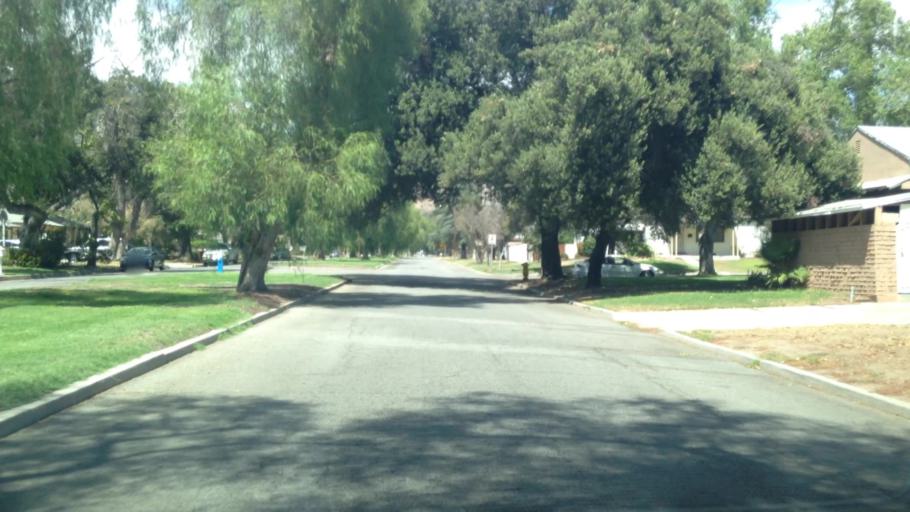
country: US
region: California
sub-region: San Bernardino County
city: San Bernardino
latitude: 34.1384
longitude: -117.3078
